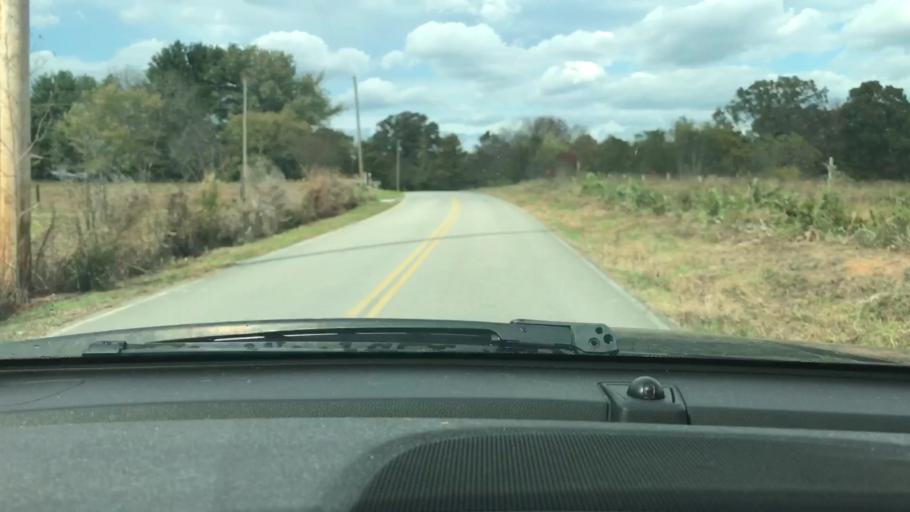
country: US
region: Tennessee
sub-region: Dickson County
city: Charlotte
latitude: 36.1956
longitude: -87.2934
